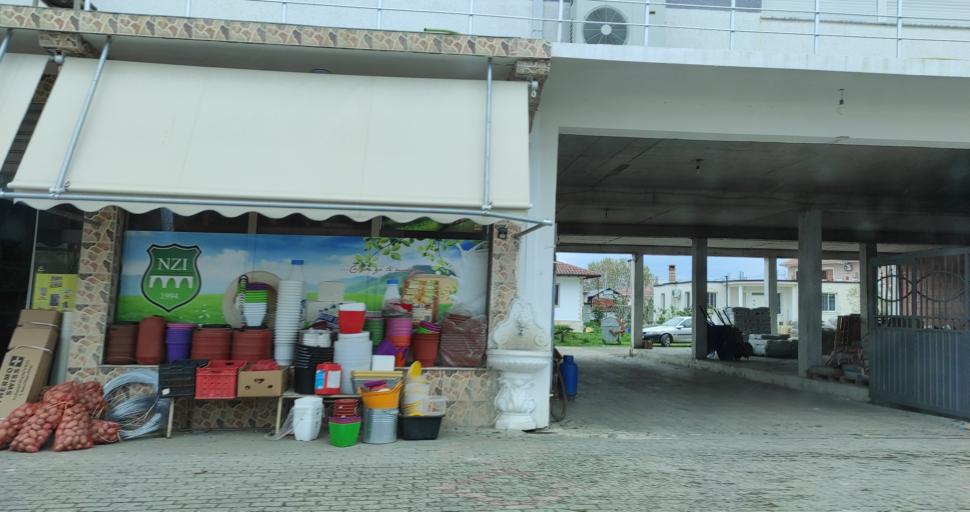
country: AL
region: Shkoder
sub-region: Rrethi i Shkodres
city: Berdica e Madhe
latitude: 41.9801
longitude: 19.4839
